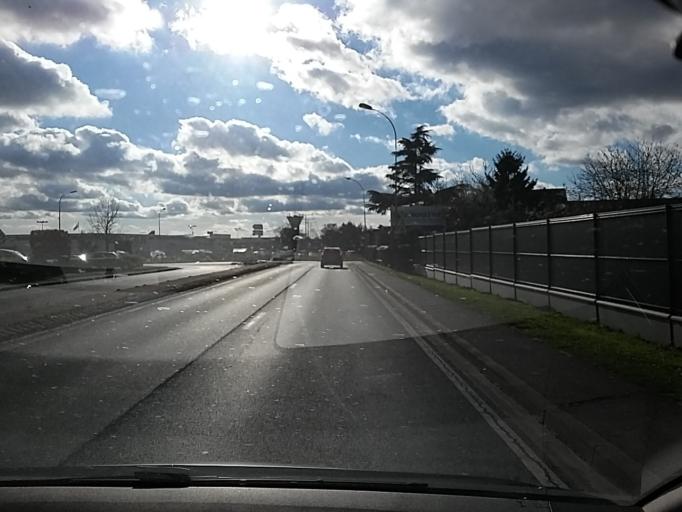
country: FR
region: Picardie
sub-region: Departement de la Somme
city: Longueau
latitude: 49.8679
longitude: 2.3705
